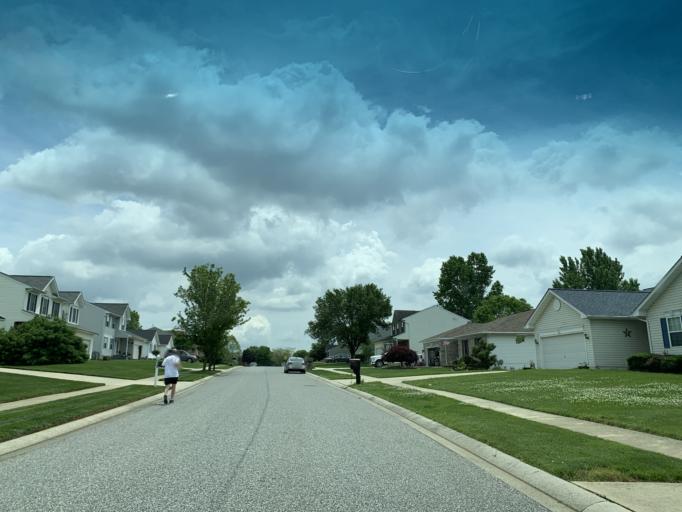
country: US
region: Maryland
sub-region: Harford County
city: South Bel Air
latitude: 39.5435
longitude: -76.3059
